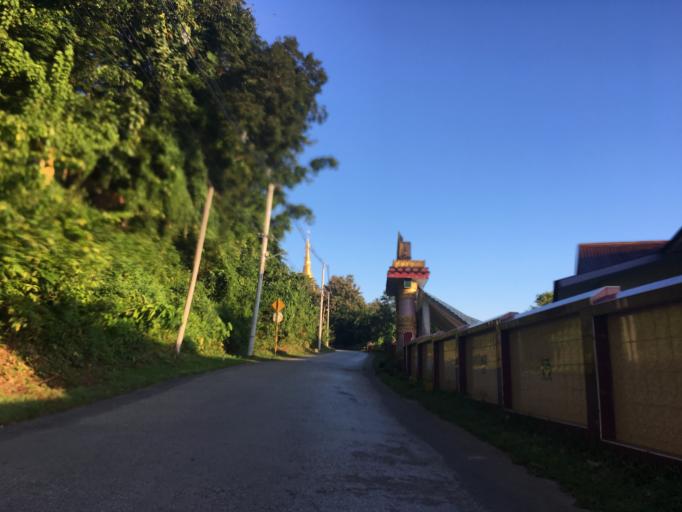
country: MM
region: Mon
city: Mawlamyine
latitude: 16.4706
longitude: 97.6310
